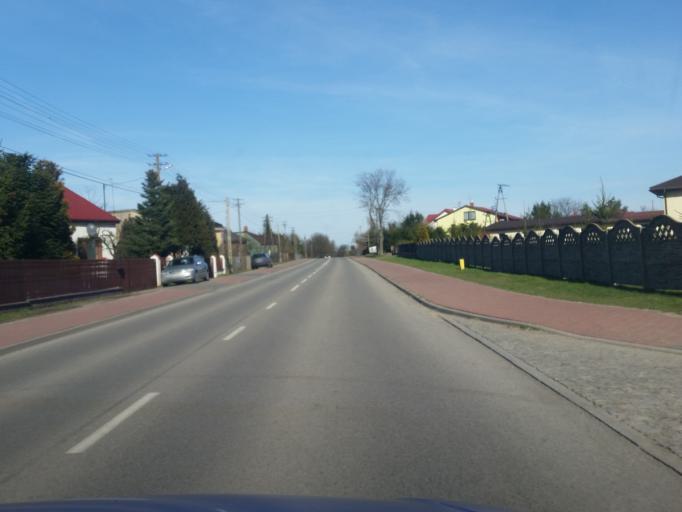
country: PL
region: Lodz Voivodeship
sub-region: Powiat radomszczanski
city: Kamiensk
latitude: 51.2038
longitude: 19.5157
